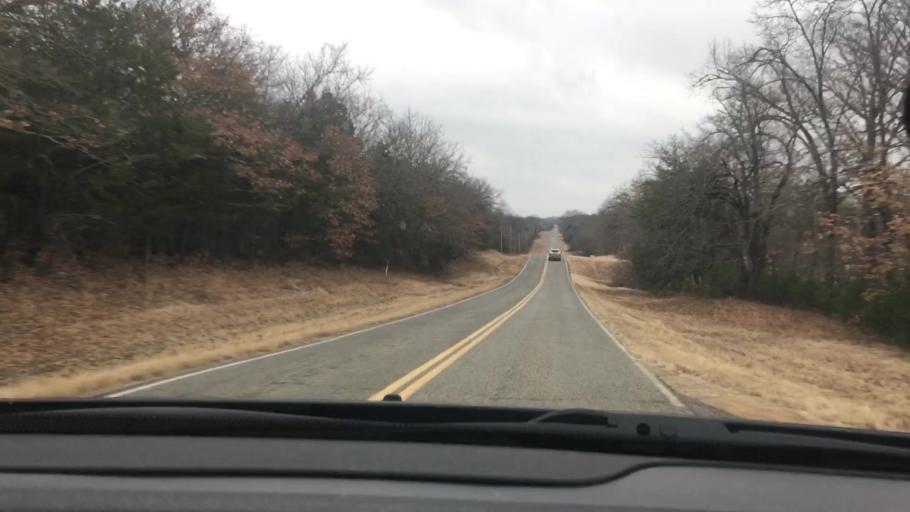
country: US
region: Oklahoma
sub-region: Johnston County
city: Tishomingo
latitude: 34.2087
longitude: -96.6012
